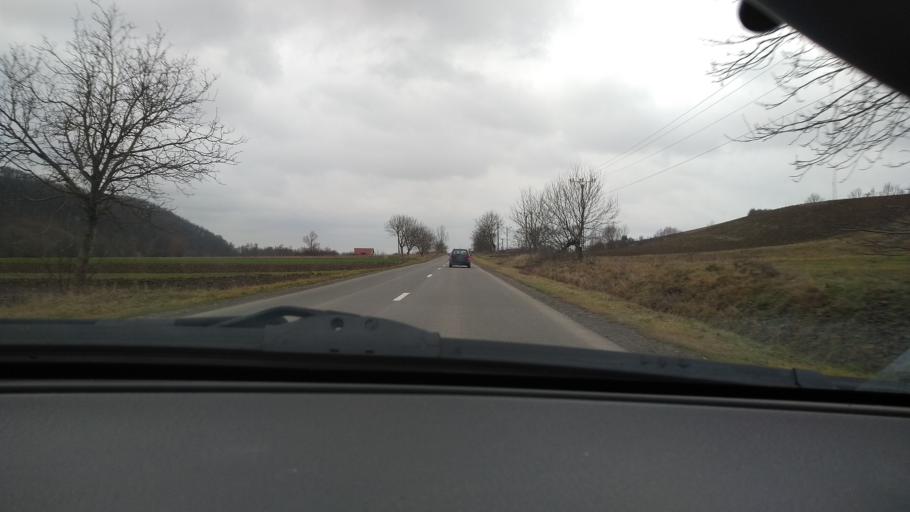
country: RO
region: Mures
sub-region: Comuna Bereni
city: Bereni
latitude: 46.5464
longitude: 24.8365
